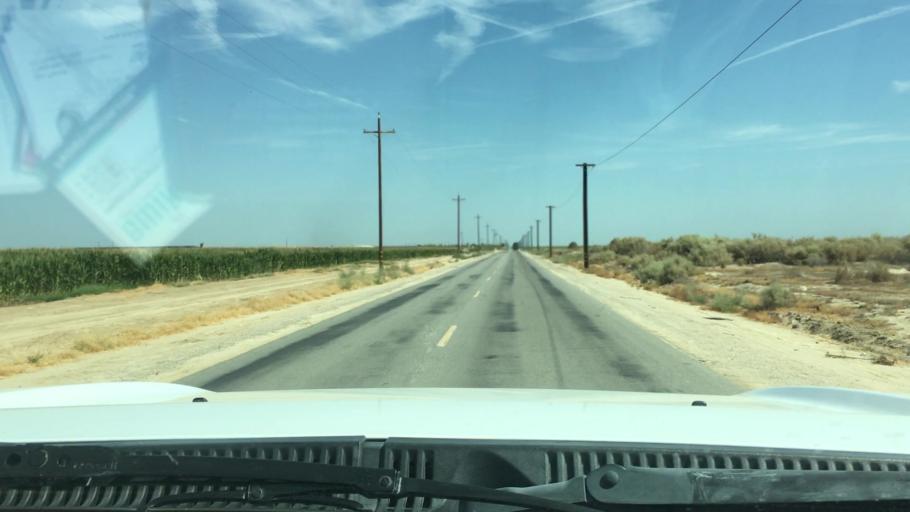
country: US
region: California
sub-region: Kern County
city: Buttonwillow
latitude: 35.4444
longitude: -119.3682
